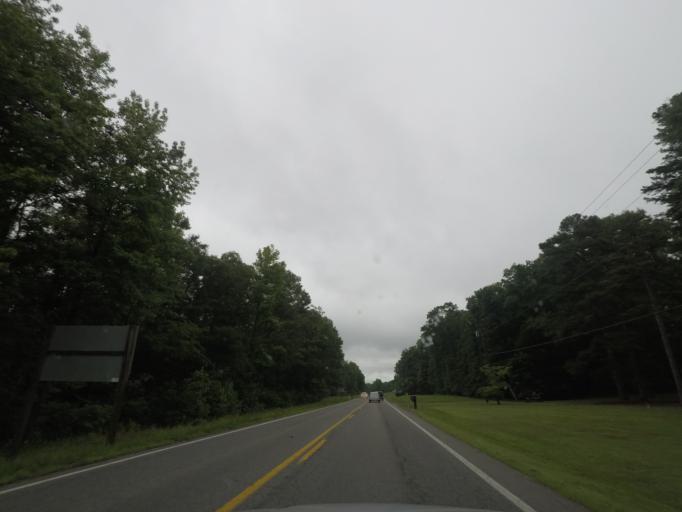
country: US
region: Virginia
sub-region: Fluvanna County
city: Weber City
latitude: 37.7839
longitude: -78.2357
